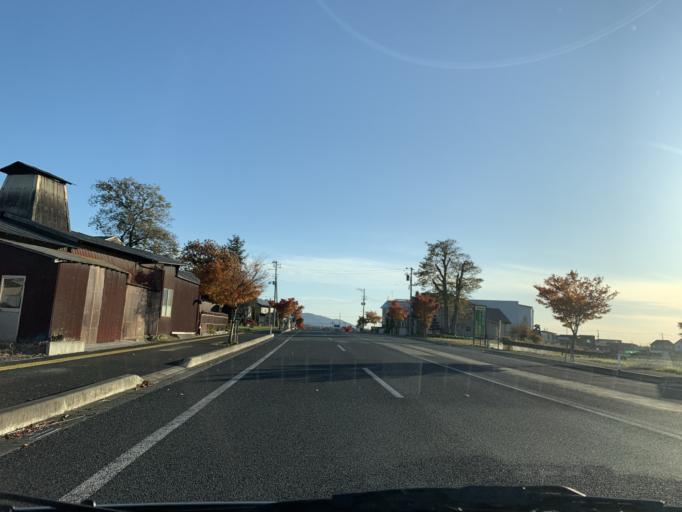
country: JP
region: Iwate
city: Mizusawa
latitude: 39.1419
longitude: 141.1841
